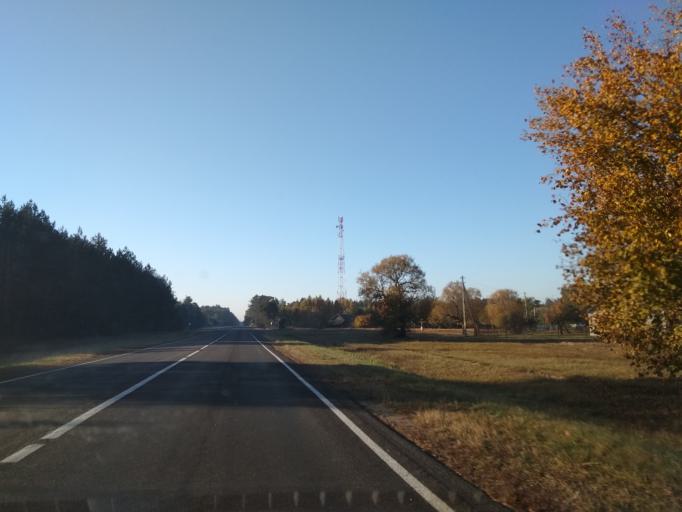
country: BY
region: Brest
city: Kobryn
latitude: 52.0548
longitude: 24.2796
